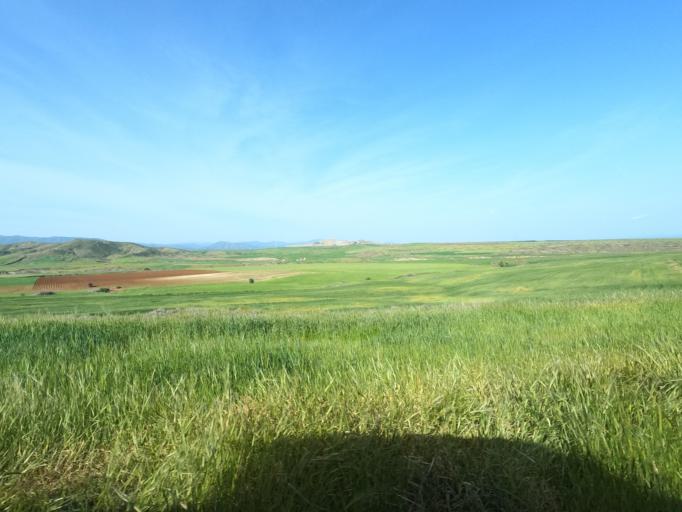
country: CY
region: Lefkosia
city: Astromeritis
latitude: 35.0944
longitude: 32.9516
